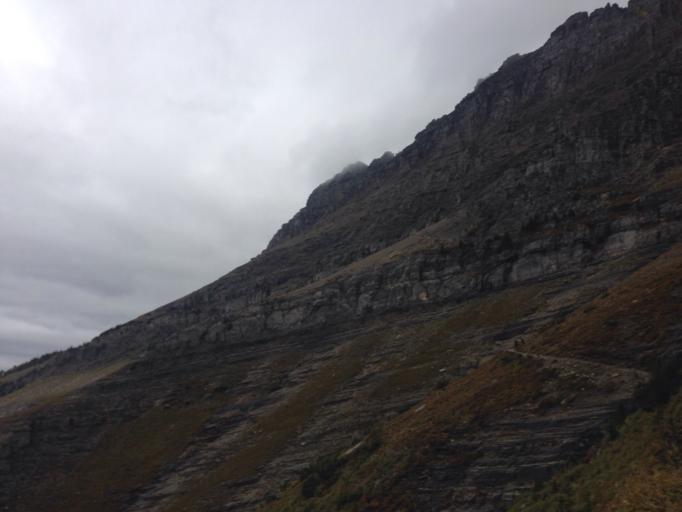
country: US
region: Montana
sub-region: Flathead County
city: Columbia Falls
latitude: 48.7412
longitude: -113.7293
